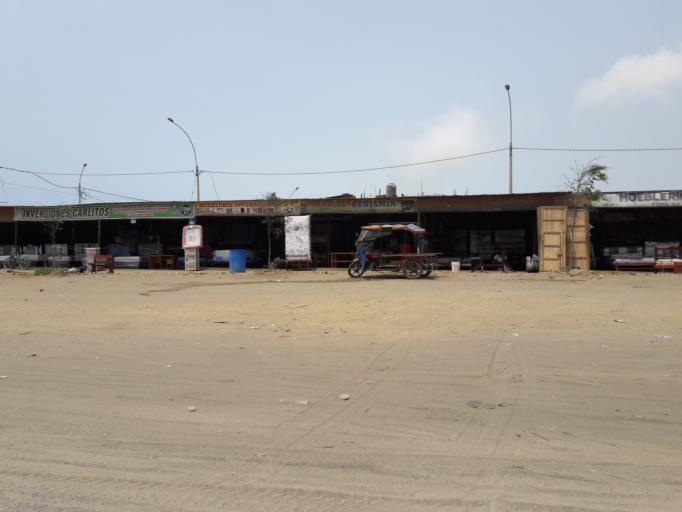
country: PE
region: Lima
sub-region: Lima
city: Santa Rosa
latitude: -11.7751
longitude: -77.1634
